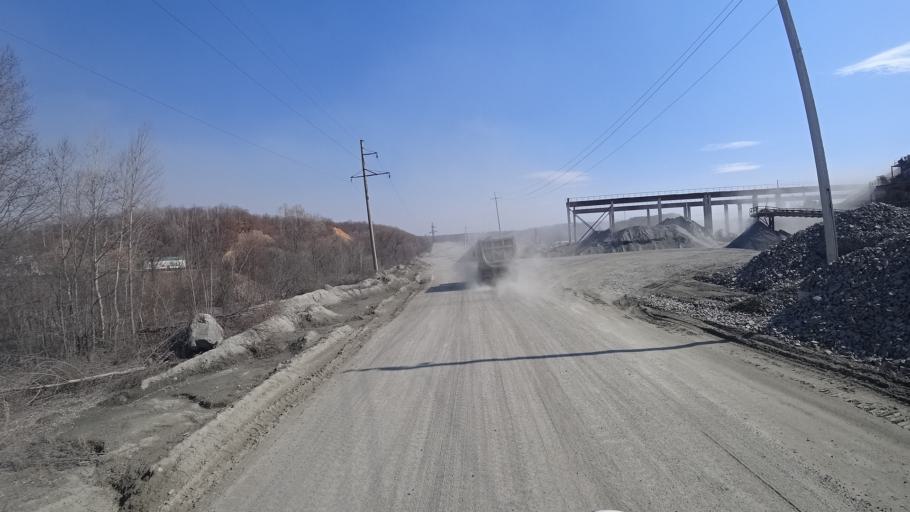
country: RU
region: Amur
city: Novobureyskiy
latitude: 49.7934
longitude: 129.9601
